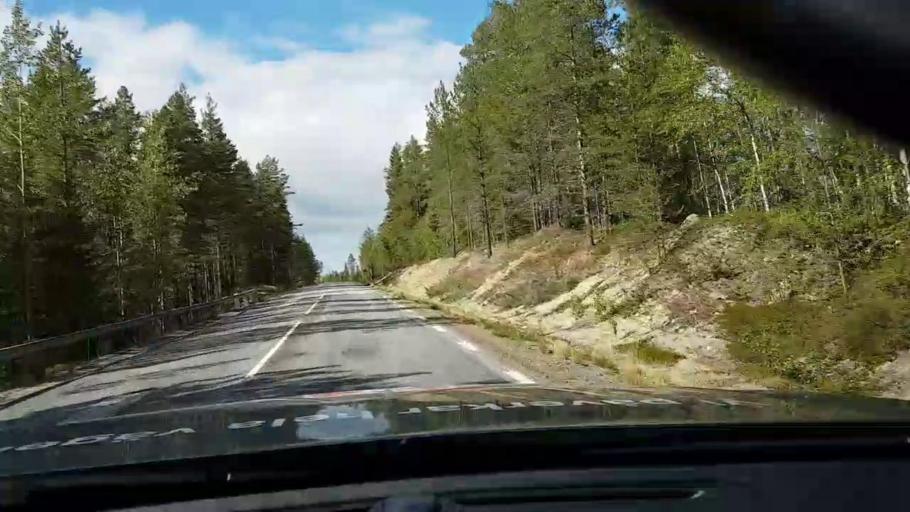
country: SE
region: Vaesterbotten
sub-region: Asele Kommun
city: Asele
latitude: 63.8405
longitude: 17.4291
